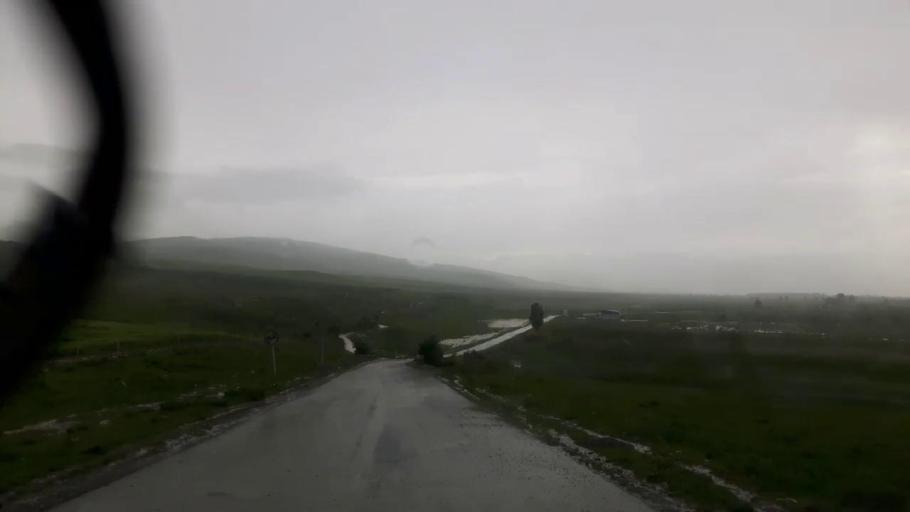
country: GE
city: Agara
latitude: 42.0140
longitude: 43.8274
